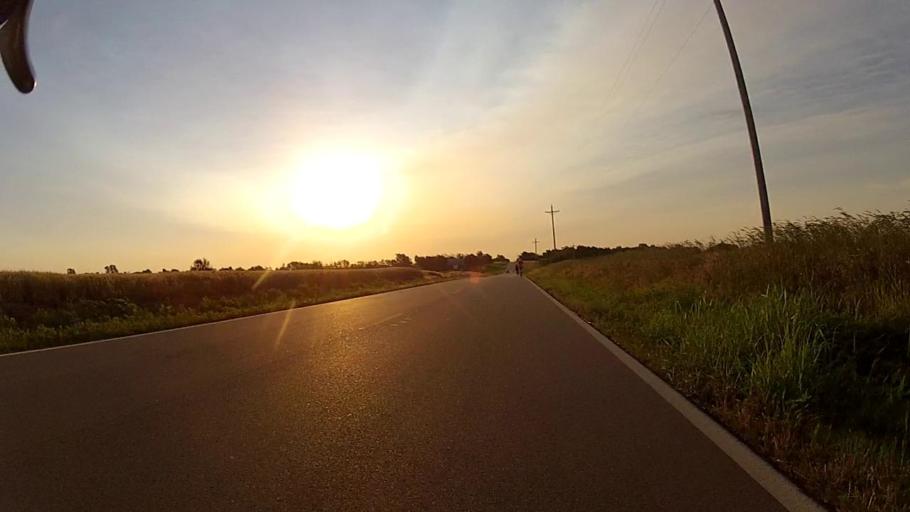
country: US
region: Kansas
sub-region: Harper County
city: Anthony
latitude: 37.1527
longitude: -97.9620
